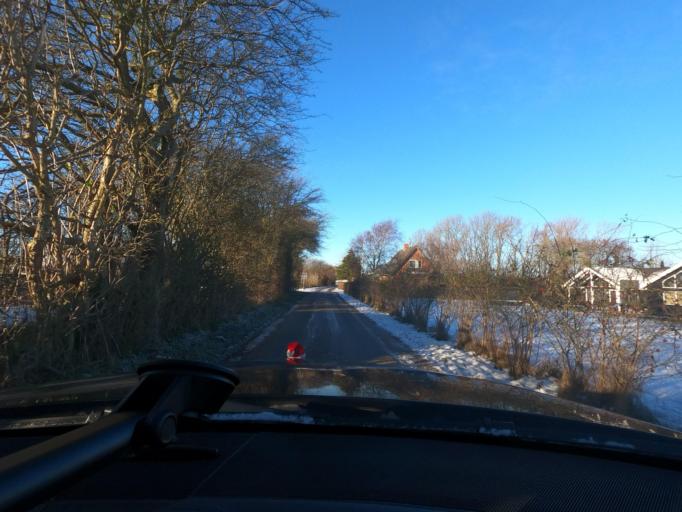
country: DK
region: South Denmark
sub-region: Sonderborg Kommune
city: Horuphav
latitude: 54.8711
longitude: 9.8891
